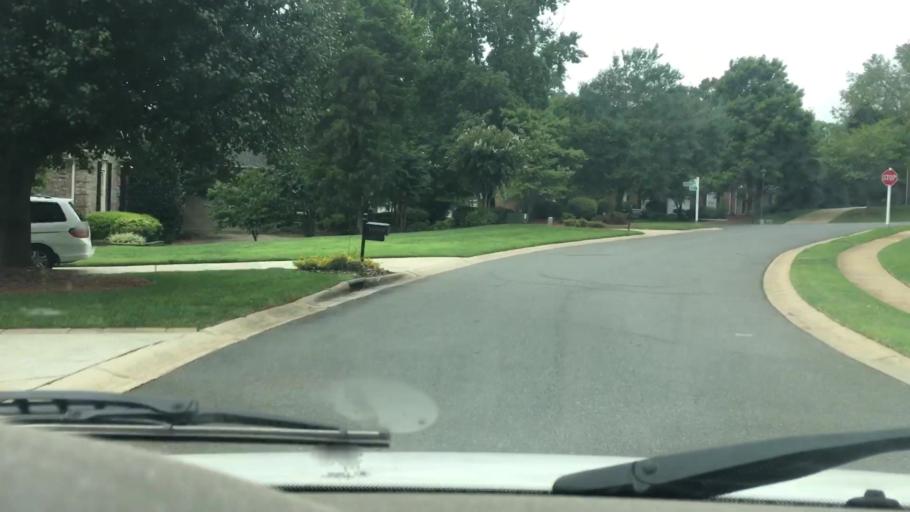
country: US
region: North Carolina
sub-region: Mecklenburg County
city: Huntersville
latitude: 35.4369
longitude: -80.8881
